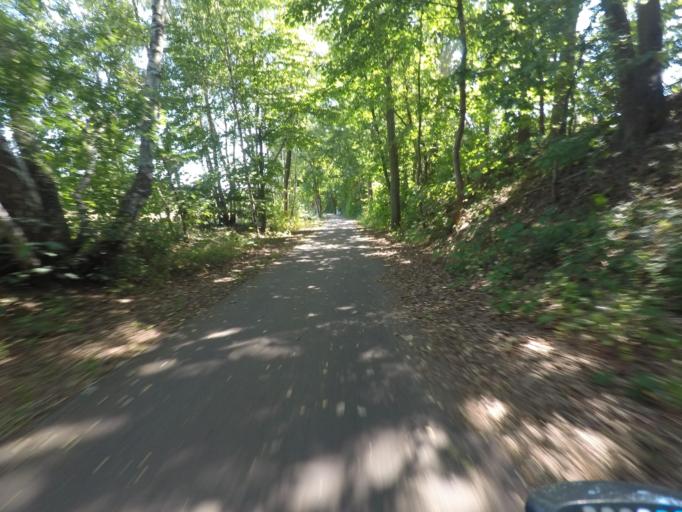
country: DE
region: Schleswig-Holstein
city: Lutjensee
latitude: 53.6383
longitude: 10.3748
